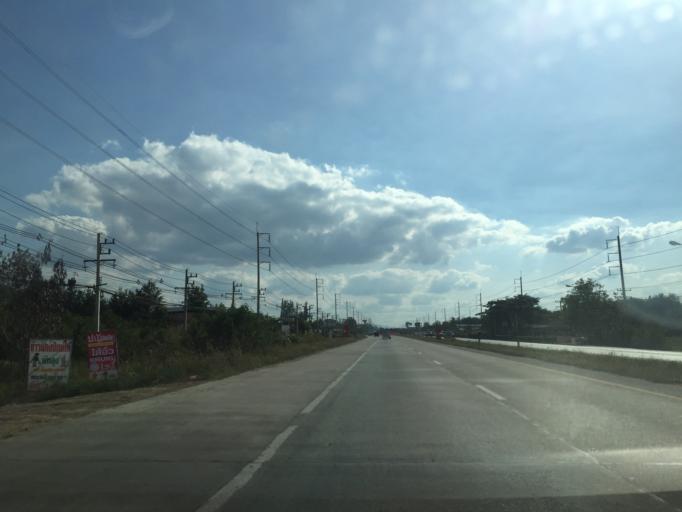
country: TH
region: Lamphun
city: Ban Thi
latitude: 18.6399
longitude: 99.0530
